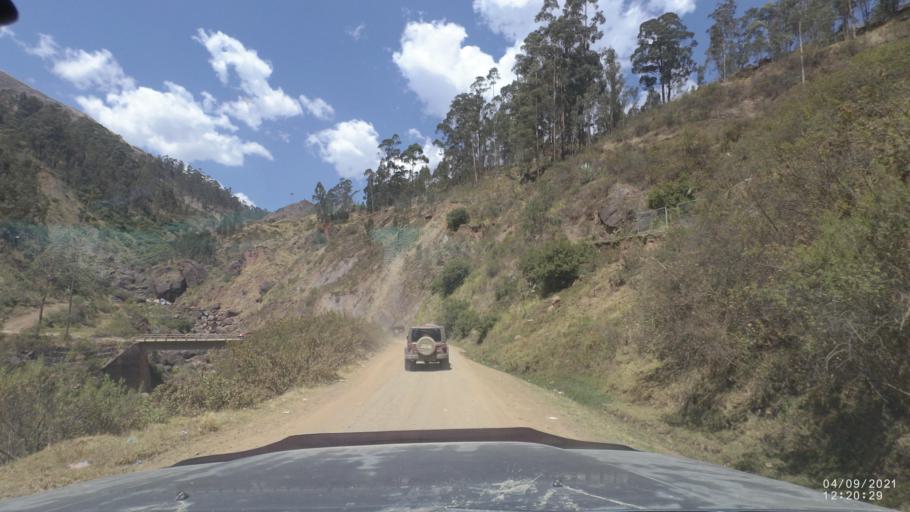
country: BO
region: Cochabamba
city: Colchani
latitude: -17.2401
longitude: -66.5274
